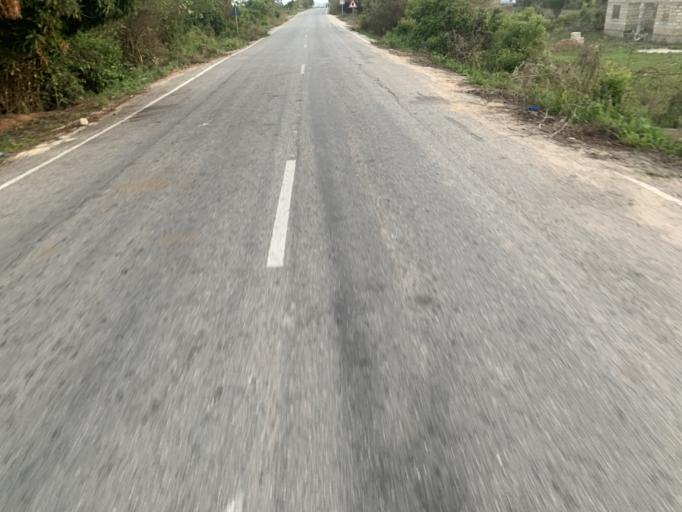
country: GH
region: Central
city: Winneba
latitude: 5.3727
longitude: -0.6070
